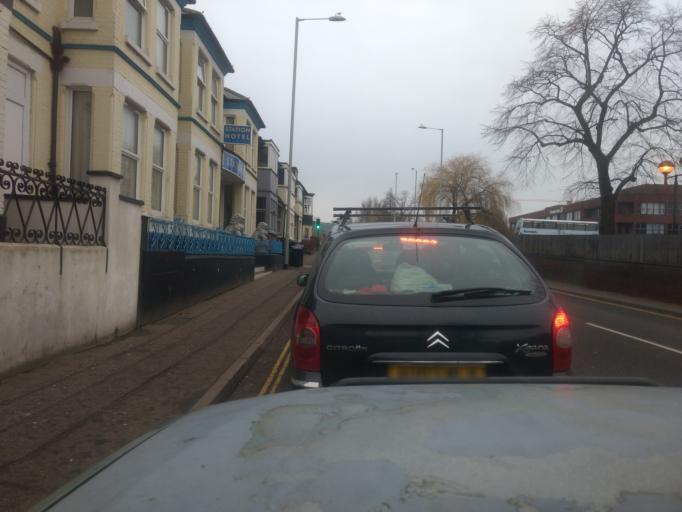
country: GB
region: England
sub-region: Norfolk
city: Thorpe Hamlet
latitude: 52.6285
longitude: 1.3066
